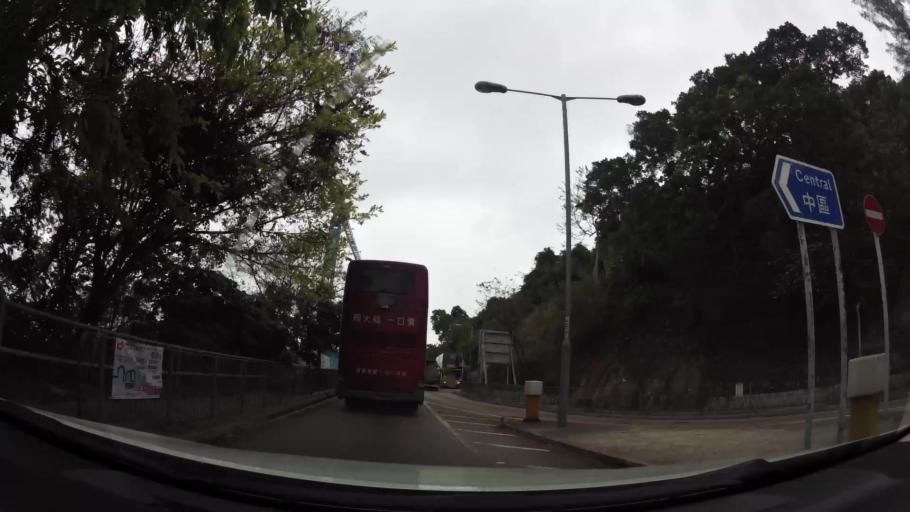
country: HK
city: Hong Kong
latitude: 22.2745
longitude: 114.1181
